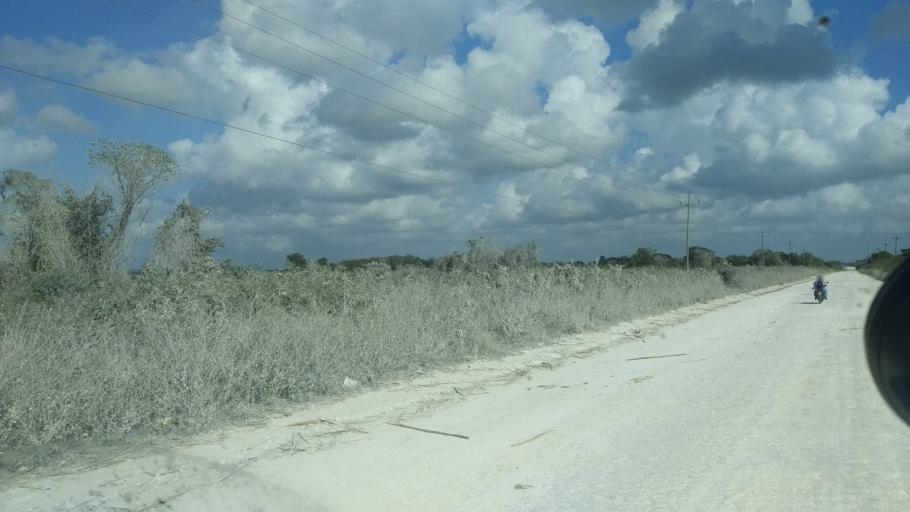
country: BZ
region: Corozal
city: Corozal
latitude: 18.3306
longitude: -88.4949
